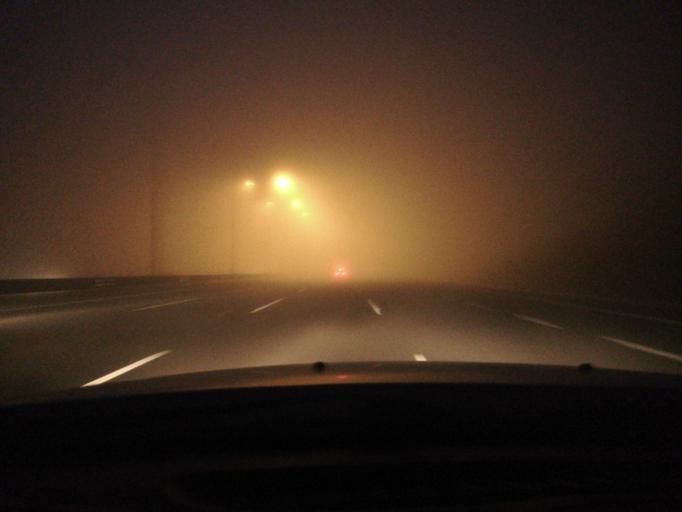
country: TR
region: Istanbul
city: Sultanbeyli
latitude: 40.9818
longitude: 29.3282
